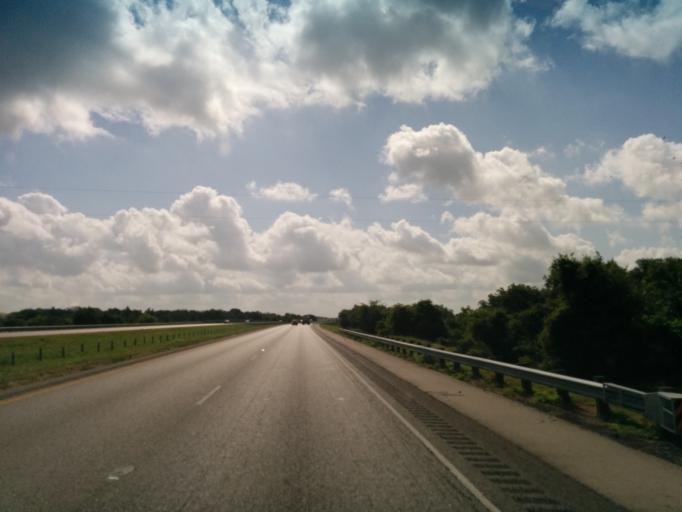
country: US
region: Texas
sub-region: Fayette County
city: Schulenburg
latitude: 29.6911
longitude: -96.9819
